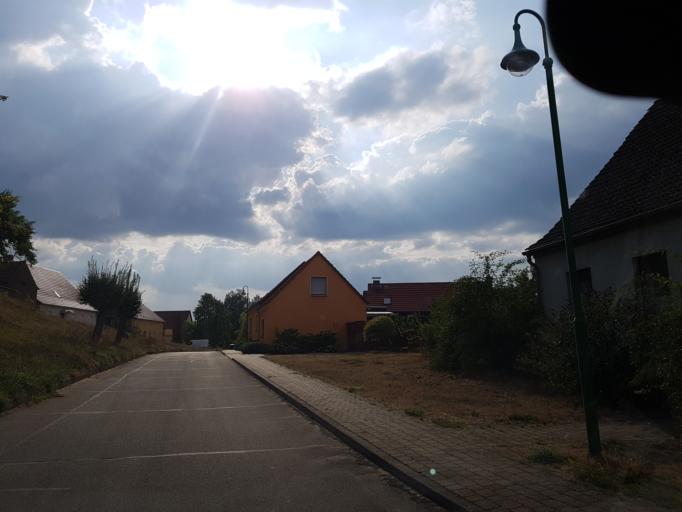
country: DE
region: Brandenburg
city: Wiesenburg
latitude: 52.0374
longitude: 12.5228
